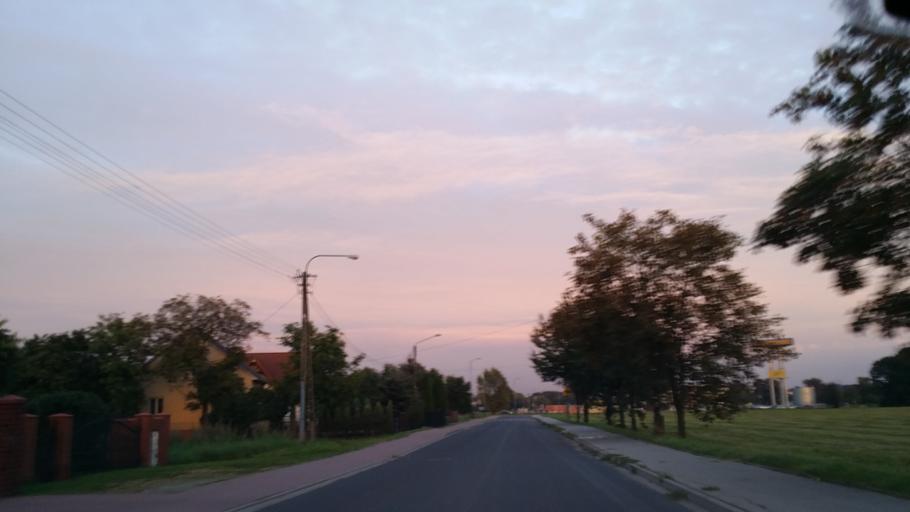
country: PL
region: Lesser Poland Voivodeship
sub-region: Powiat oswiecimski
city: Zaborze
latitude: 50.0257
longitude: 19.2265
